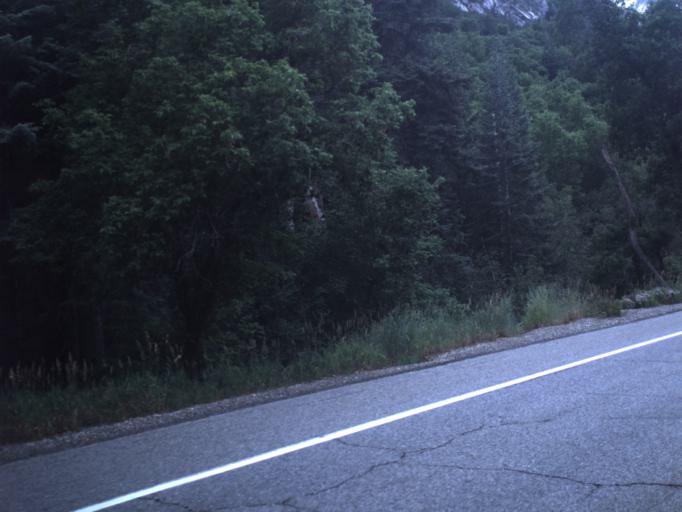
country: US
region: Utah
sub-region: Salt Lake County
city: Granite
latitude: 40.5711
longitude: -111.7444
